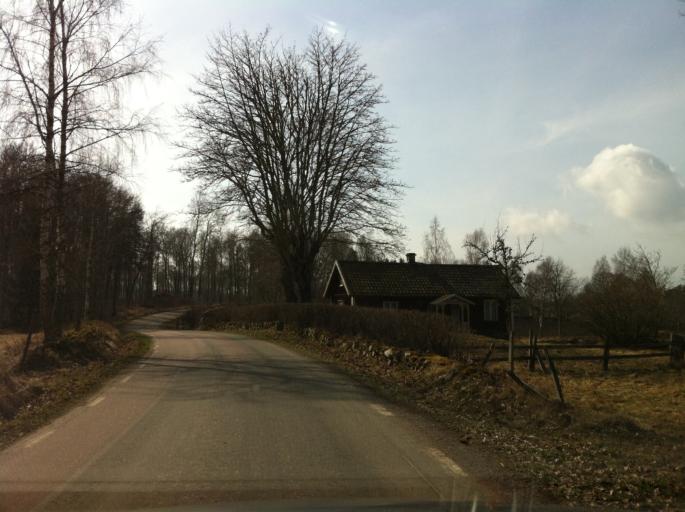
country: SE
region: Vaestra Goetaland
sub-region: Falkopings Kommun
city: Falkoeping
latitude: 58.2384
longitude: 13.5073
